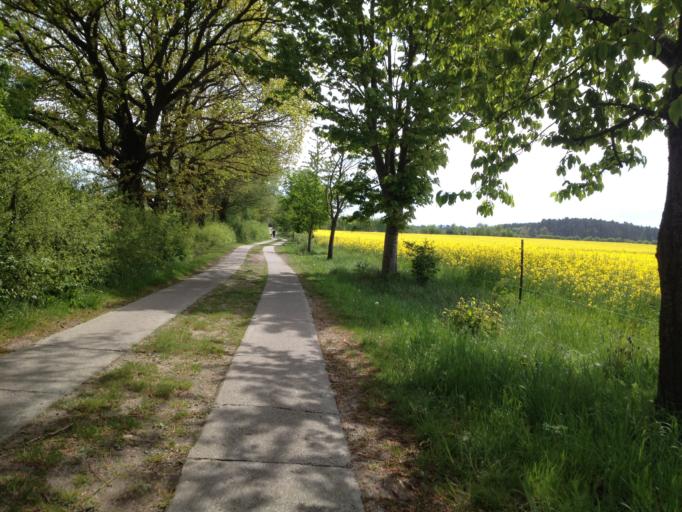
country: DE
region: Brandenburg
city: Lychen
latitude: 53.2751
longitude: 13.3775
